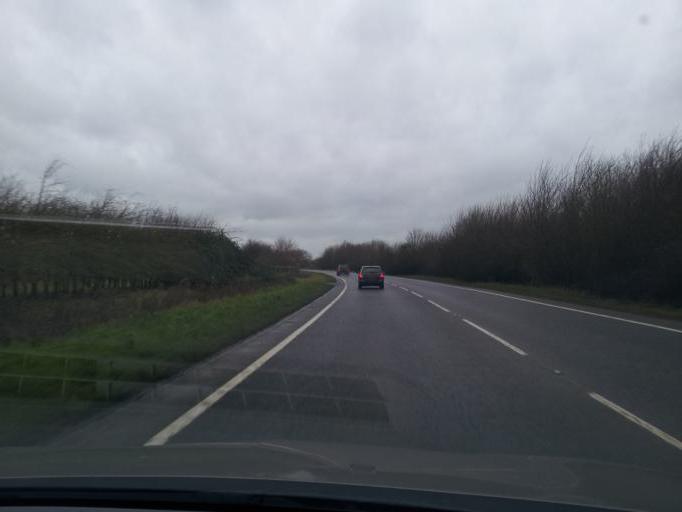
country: GB
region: England
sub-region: Norfolk
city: Diss
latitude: 52.3619
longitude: 1.1436
